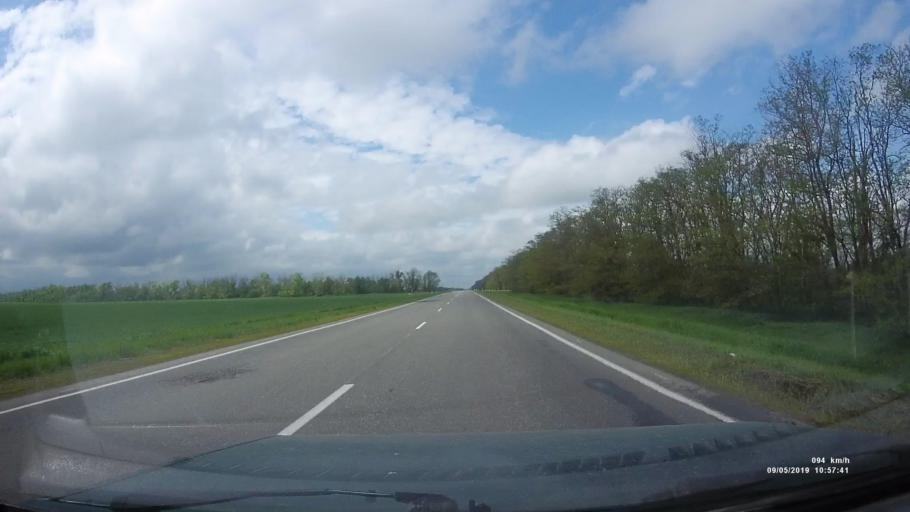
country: RU
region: Rostov
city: Peshkovo
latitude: 46.8644
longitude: 39.2742
